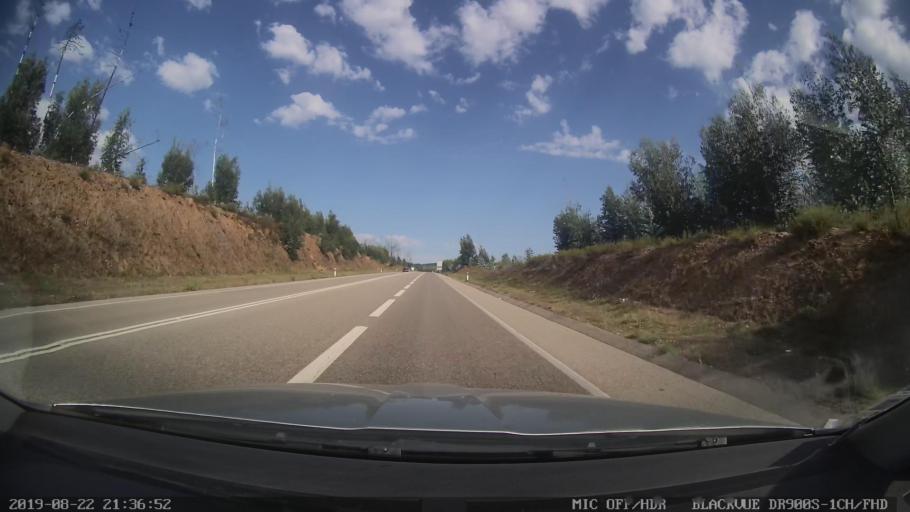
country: PT
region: Leiria
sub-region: Figueiro Dos Vinhos
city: Figueiro dos Vinhos
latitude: 39.9267
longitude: -8.2372
